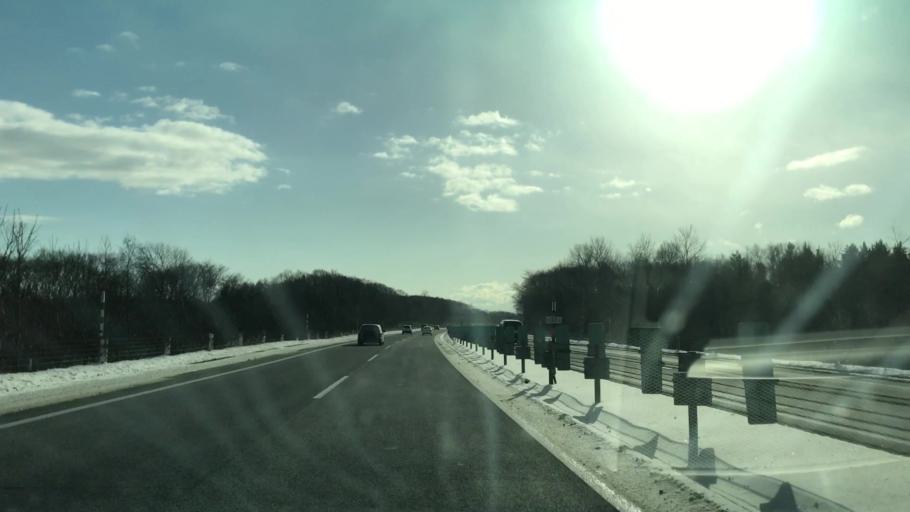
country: JP
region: Hokkaido
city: Chitose
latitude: 42.8359
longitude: 141.6067
